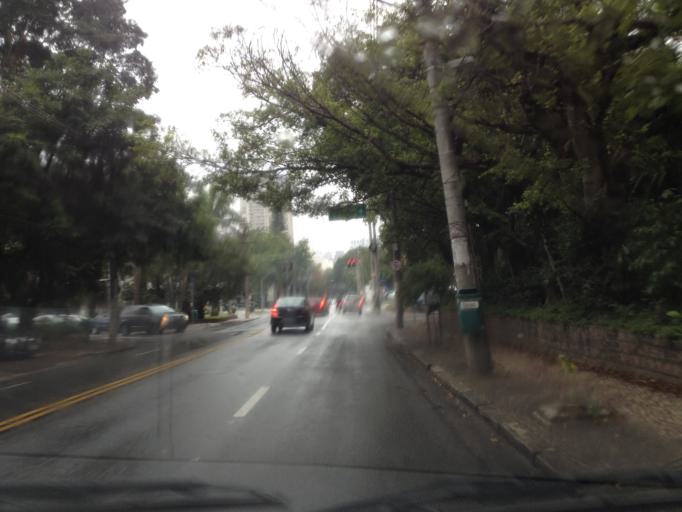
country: BR
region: Sao Paulo
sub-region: Sao Paulo
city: Sao Paulo
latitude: -23.5700
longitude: -46.6726
